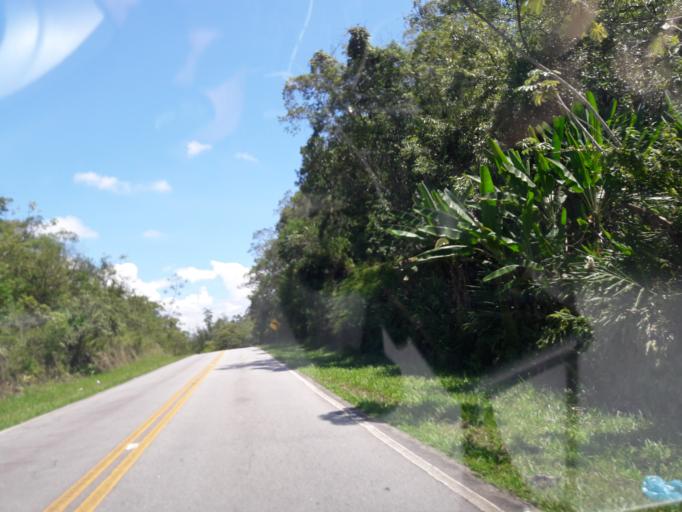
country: BR
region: Parana
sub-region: Antonina
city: Antonina
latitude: -25.5241
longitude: -48.7721
